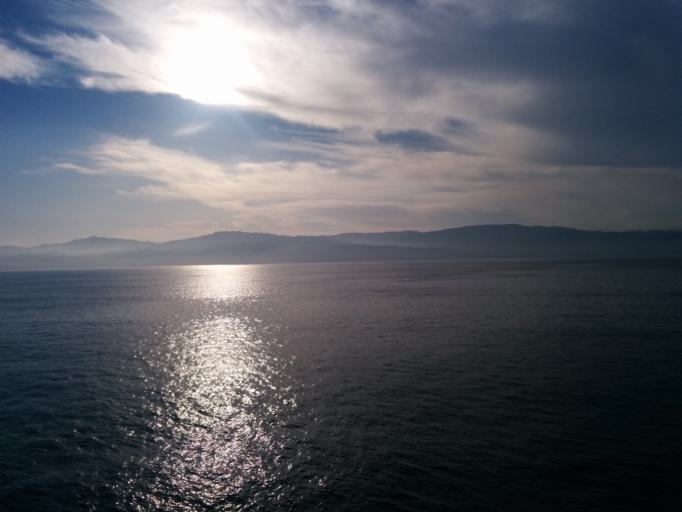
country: MA
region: Tanger-Tetouan
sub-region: Tanger-Assilah
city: Tangier
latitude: 35.8036
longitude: -5.7848
